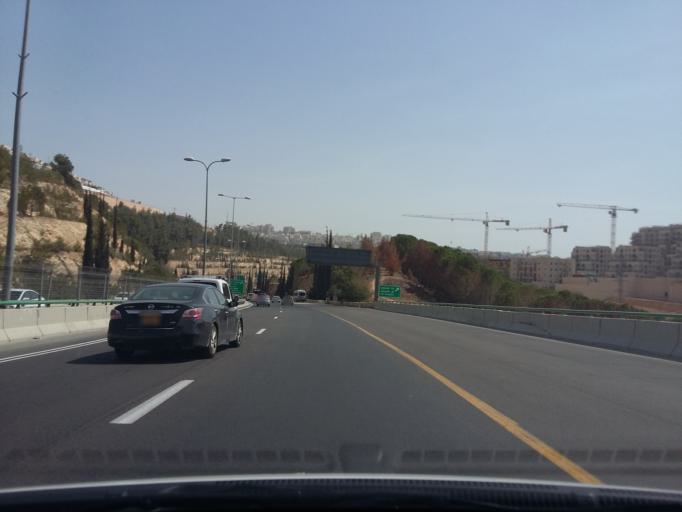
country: PS
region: West Bank
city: Bayt Iksa
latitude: 31.8178
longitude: 35.2122
